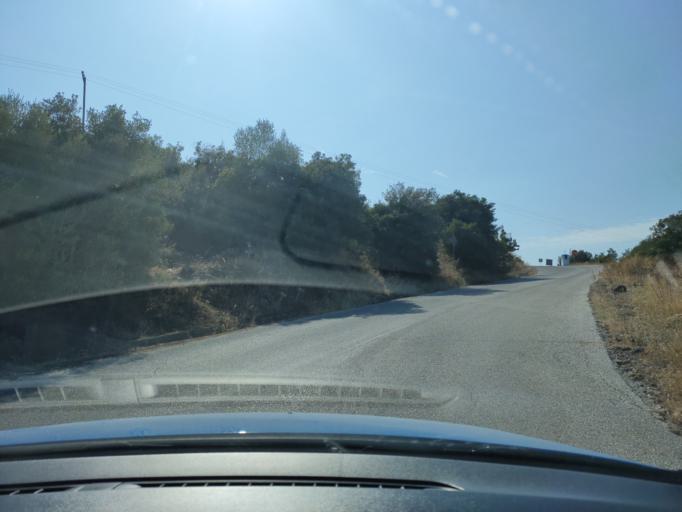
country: GR
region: North Aegean
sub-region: Nomos Lesvou
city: Mantamados
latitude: 39.3716
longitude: 26.3050
